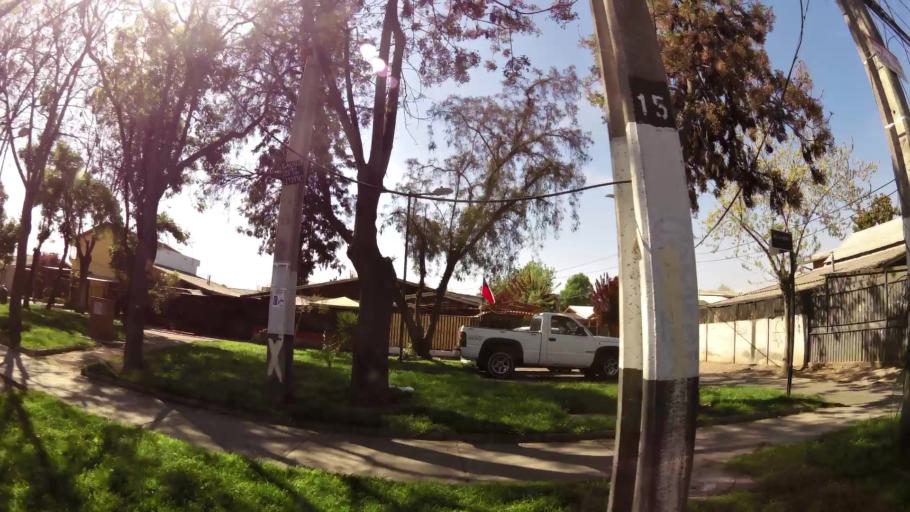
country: CL
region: Santiago Metropolitan
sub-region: Provincia de Santiago
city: Villa Presidente Frei, Nunoa, Santiago, Chile
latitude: -33.4992
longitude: -70.5777
